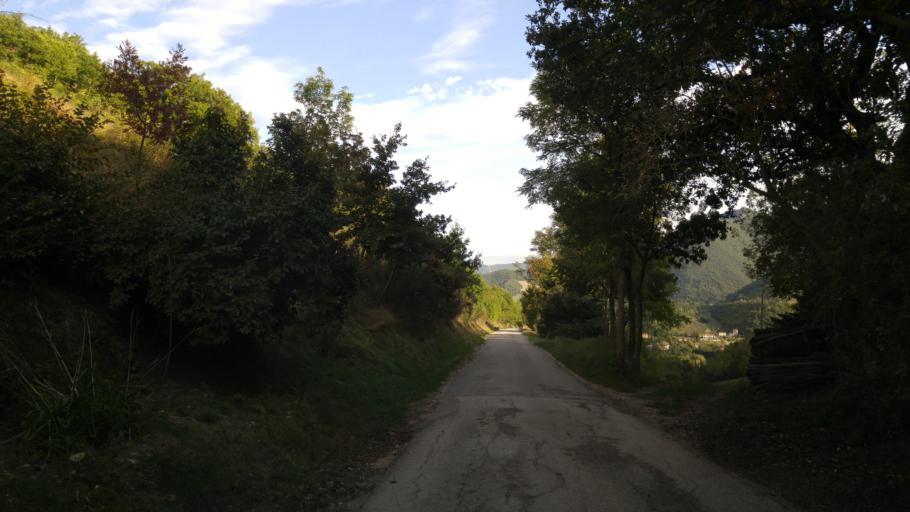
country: IT
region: The Marches
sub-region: Provincia di Pesaro e Urbino
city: Cagli
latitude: 43.5531
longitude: 12.6318
